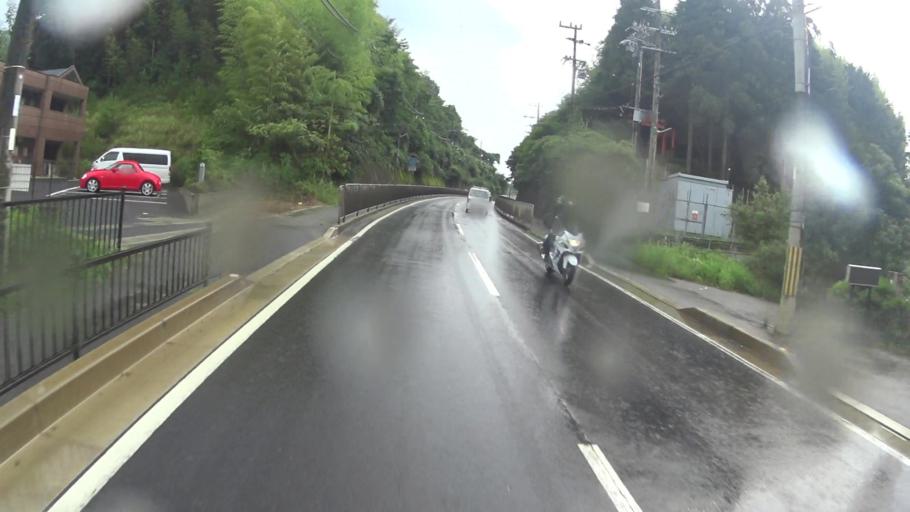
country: JP
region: Kyoto
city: Uji
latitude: 34.8507
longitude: 135.8584
